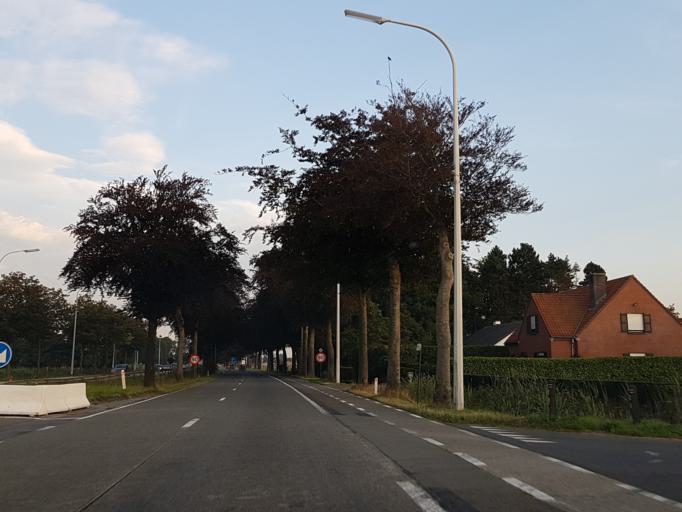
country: BE
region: Flanders
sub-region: Provincie Oost-Vlaanderen
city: Maldegem
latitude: 51.2247
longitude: 3.4052
